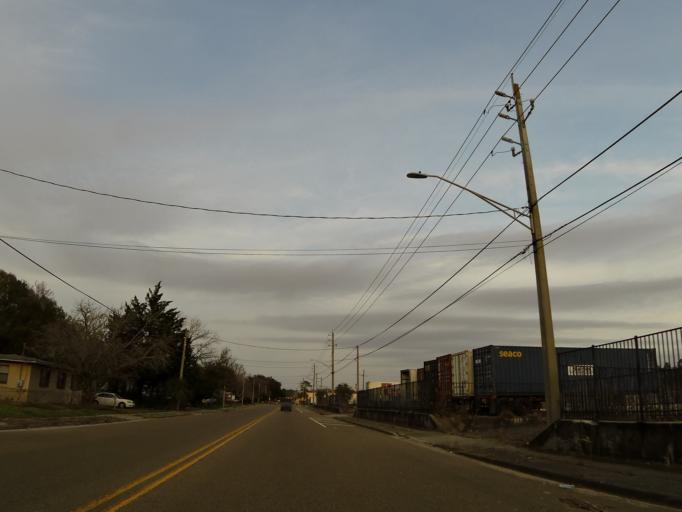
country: US
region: Florida
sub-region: Duval County
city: Jacksonville
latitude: 30.3678
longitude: -81.7153
